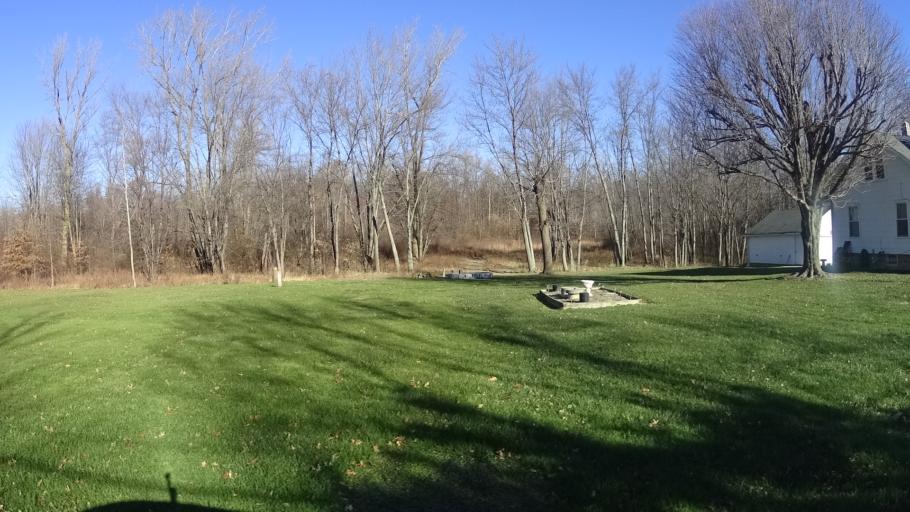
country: US
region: Ohio
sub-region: Lorain County
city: Sheffield
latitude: 41.4100
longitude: -82.1221
